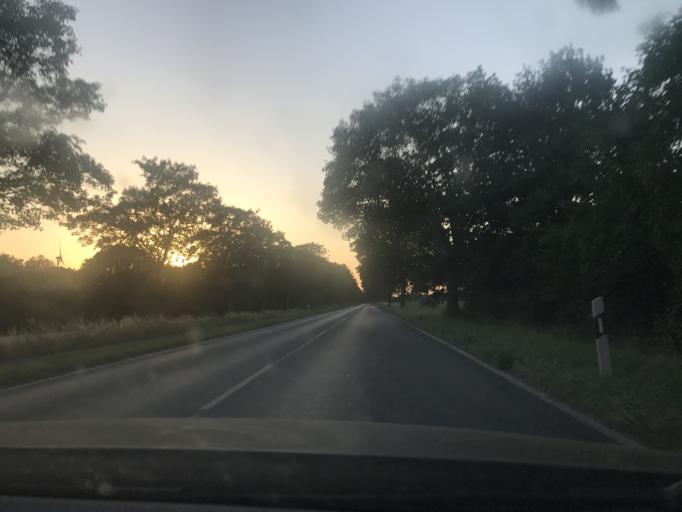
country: DE
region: North Rhine-Westphalia
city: Rheinberg
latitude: 51.5155
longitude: 6.6089
